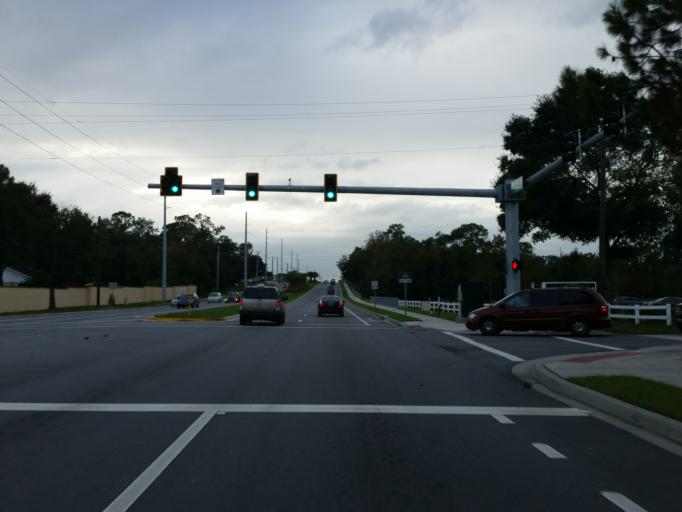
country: US
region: Florida
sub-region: Hillsborough County
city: Riverview
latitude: 27.8536
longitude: -82.2778
